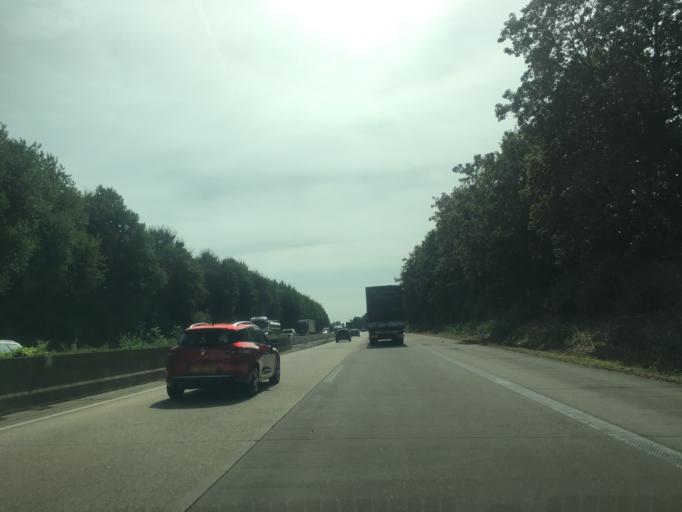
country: DE
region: North Rhine-Westphalia
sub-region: Regierungsbezirk Koln
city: Titz
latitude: 51.0233
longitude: 6.4845
